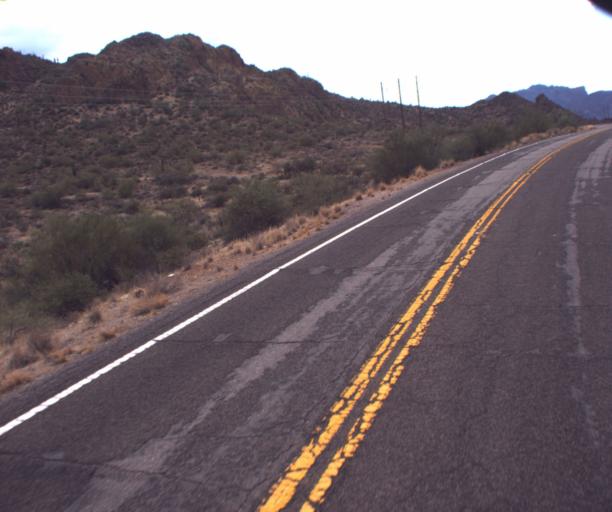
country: US
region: Arizona
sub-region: Pinal County
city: Apache Junction
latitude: 33.5142
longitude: -111.4568
